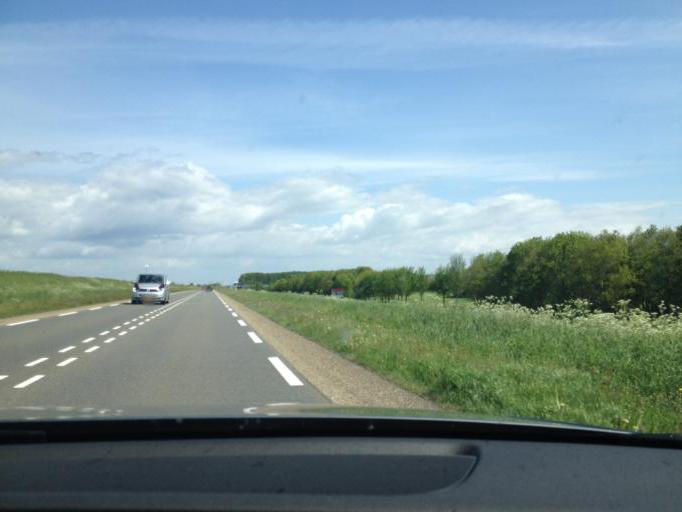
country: NL
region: Flevoland
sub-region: Gemeente Lelystad
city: Lelystad
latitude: 52.5391
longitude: 5.4509
